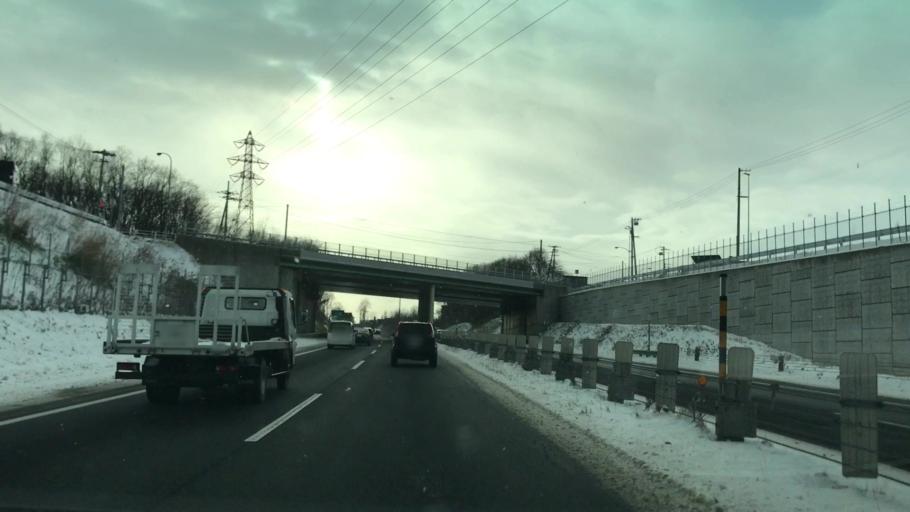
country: JP
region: Hokkaido
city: Kitahiroshima
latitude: 42.9847
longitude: 141.4719
